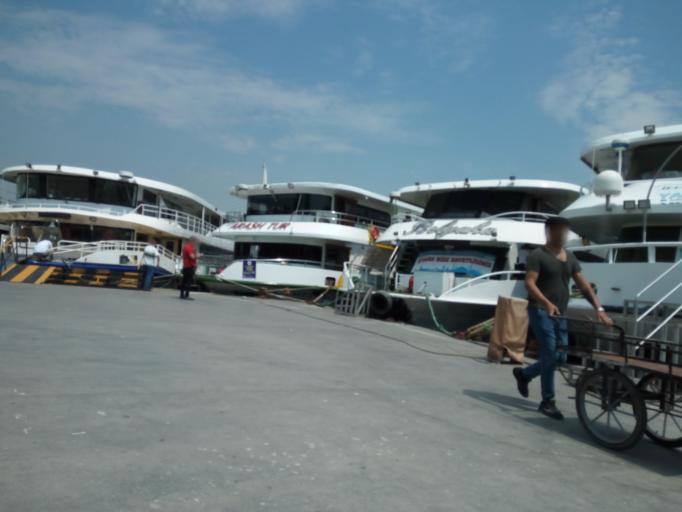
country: TR
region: Istanbul
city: Eminoenue
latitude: 41.0195
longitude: 28.9674
